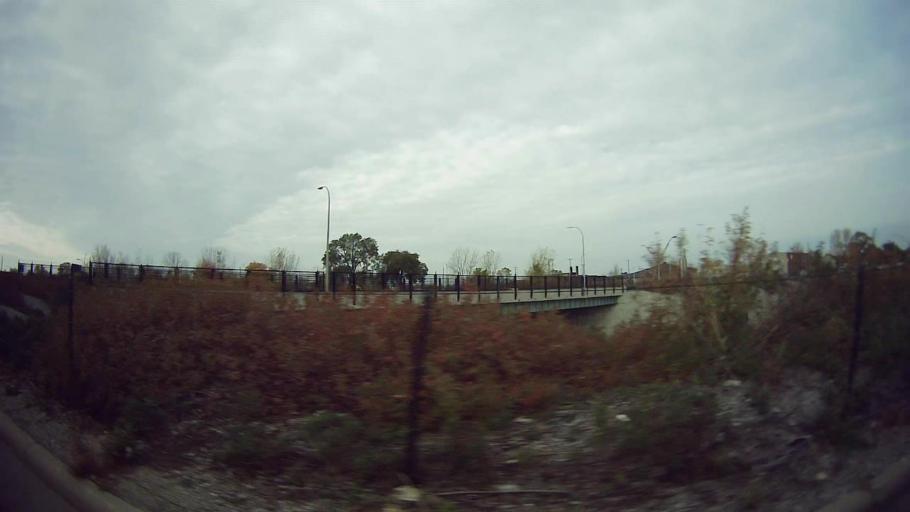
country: US
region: Michigan
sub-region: Wayne County
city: Hamtramck
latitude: 42.3956
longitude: -83.0677
